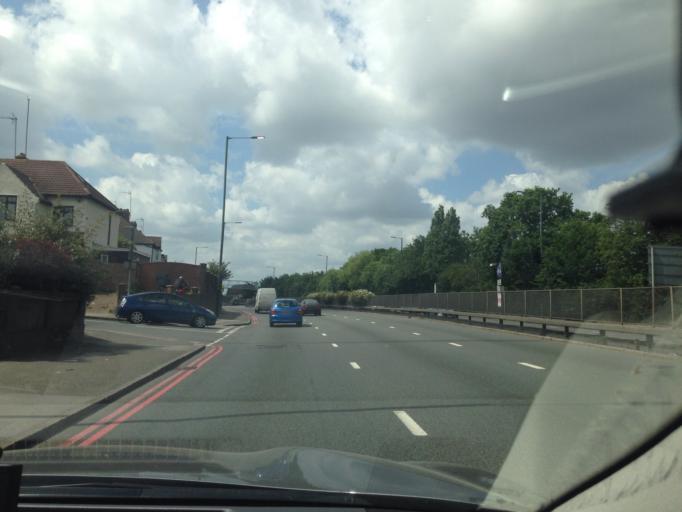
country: GB
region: England
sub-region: Greater London
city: Hendon
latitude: 51.5661
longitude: -0.2478
